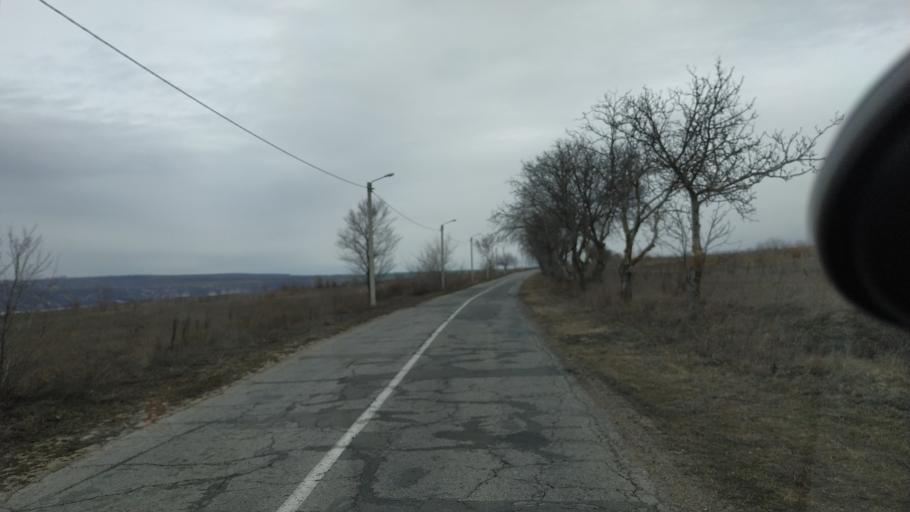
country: MD
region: Telenesti
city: Cocieri
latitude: 47.3277
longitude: 29.0967
